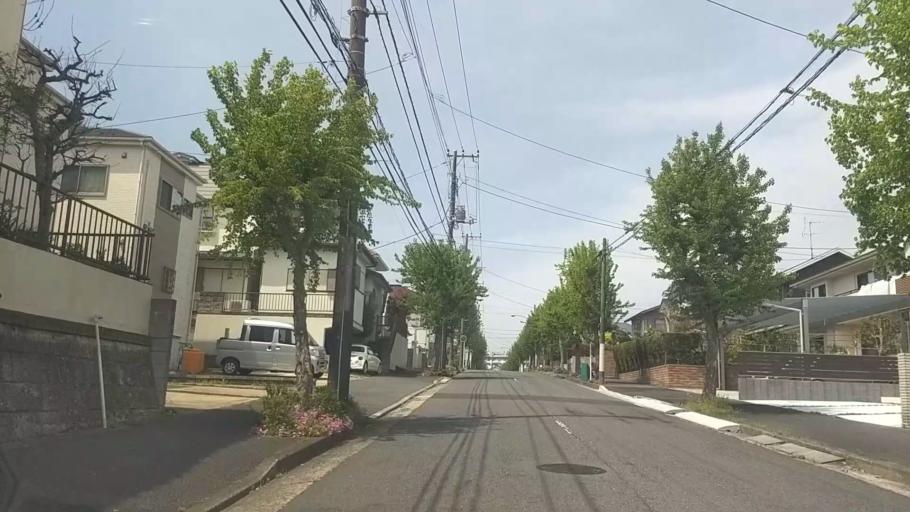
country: JP
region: Kanagawa
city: Yokohama
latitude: 35.3862
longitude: 139.5990
